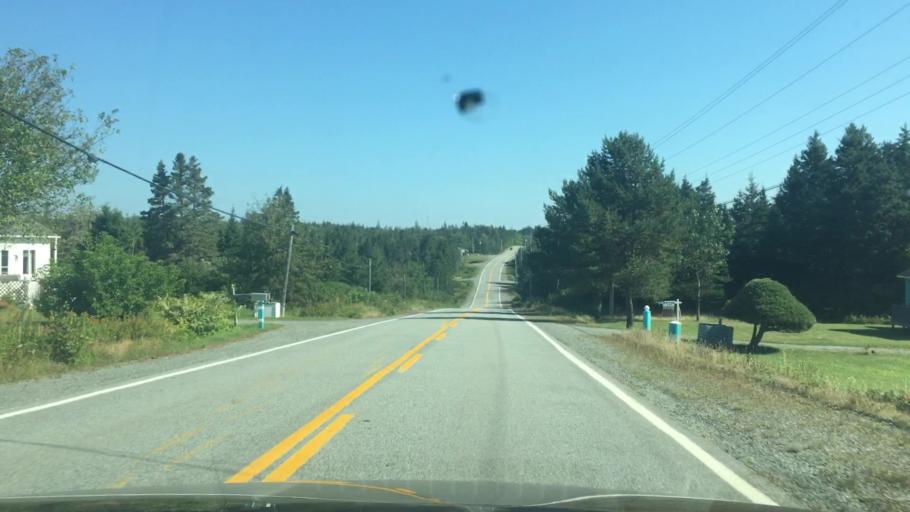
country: CA
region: Nova Scotia
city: Cole Harbour
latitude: 44.7996
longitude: -62.7155
